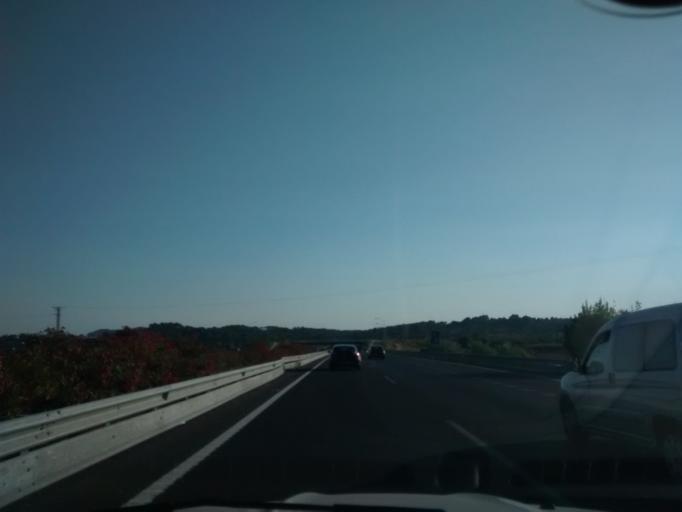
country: ES
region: Balearic Islands
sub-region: Illes Balears
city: sa Pobla
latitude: 39.7837
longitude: 3.0004
